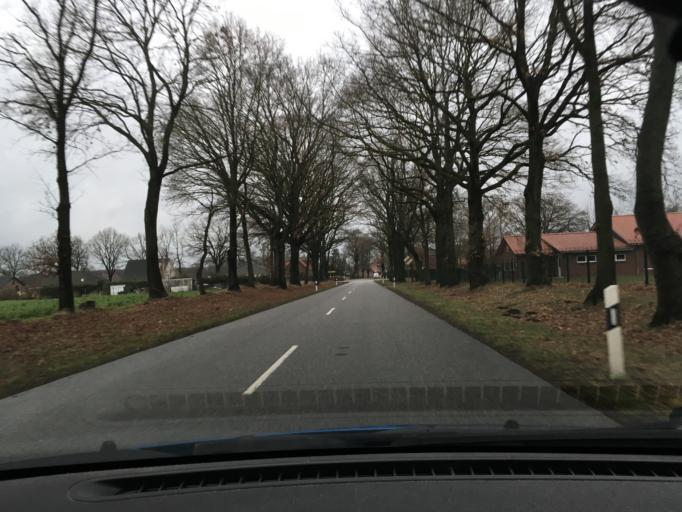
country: DE
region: Mecklenburg-Vorpommern
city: Nostorf
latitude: 53.4276
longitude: 10.6840
